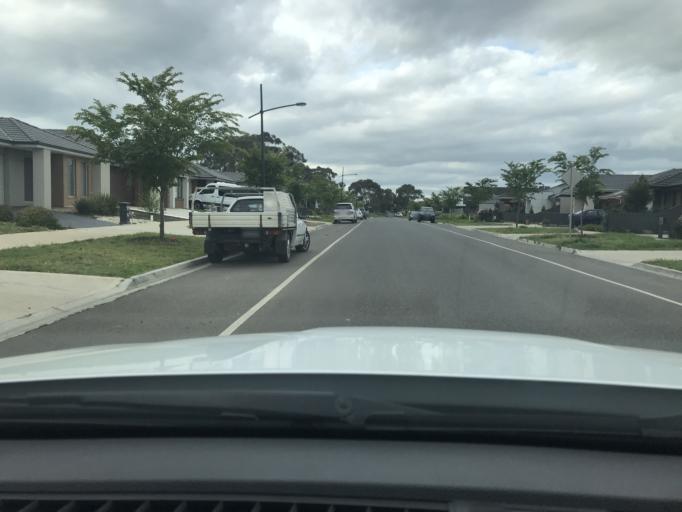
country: AU
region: Victoria
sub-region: Hume
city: Greenvale
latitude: -37.5943
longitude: 144.8879
